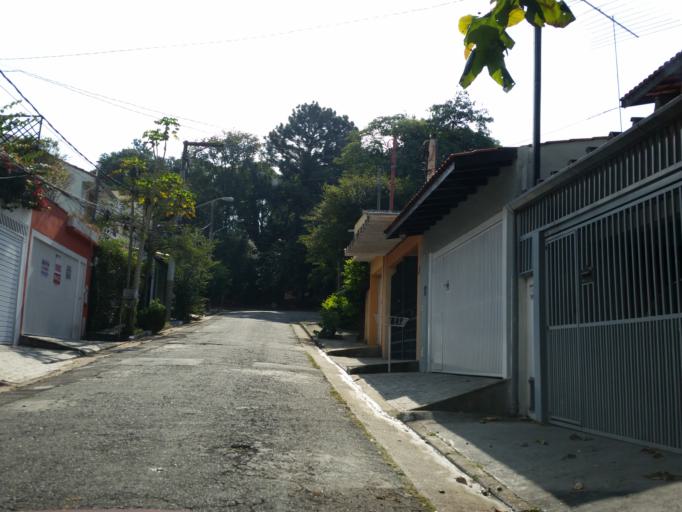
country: BR
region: Sao Paulo
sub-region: Diadema
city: Diadema
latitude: -23.6525
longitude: -46.6972
